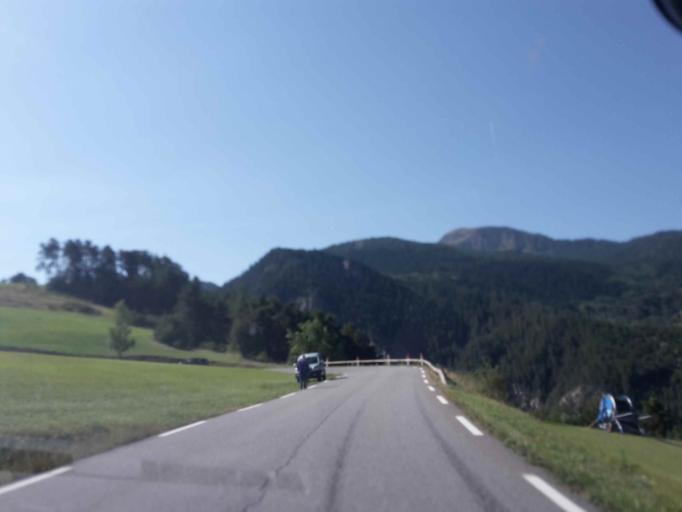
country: FR
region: Provence-Alpes-Cote d'Azur
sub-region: Departement des Hautes-Alpes
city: Guillestre
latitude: 44.6370
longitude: 6.6685
